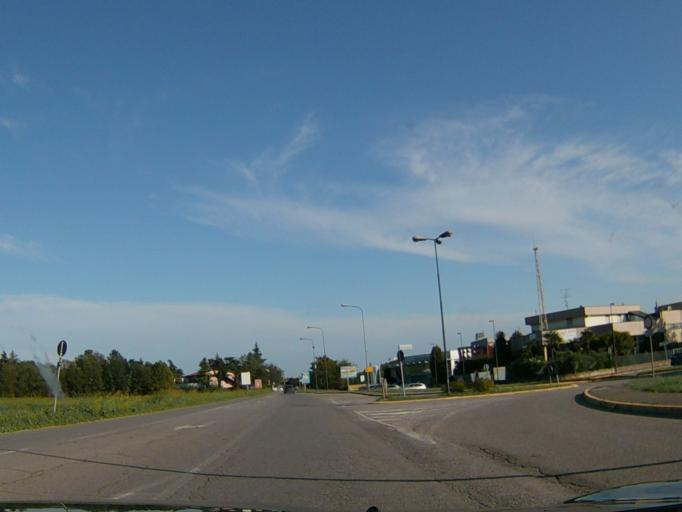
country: IT
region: Lombardy
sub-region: Provincia di Brescia
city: Molinetto
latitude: 45.4893
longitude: 10.3663
